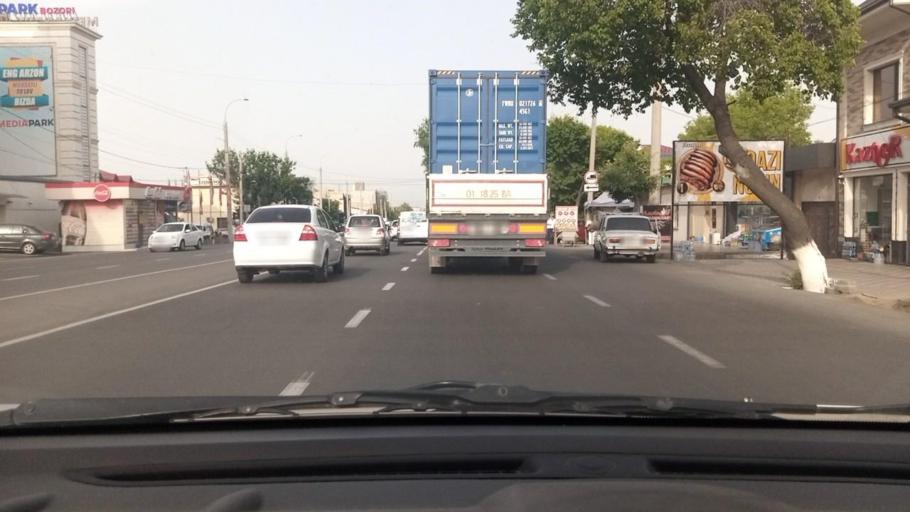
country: UZ
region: Toshkent
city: Salor
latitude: 41.3326
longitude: 69.2974
